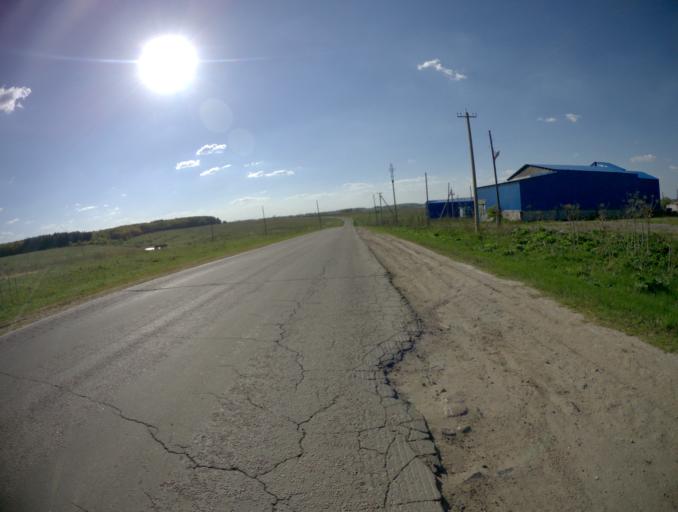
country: RU
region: Ivanovo
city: Gavrilov Posad
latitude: 56.3458
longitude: 40.1834
